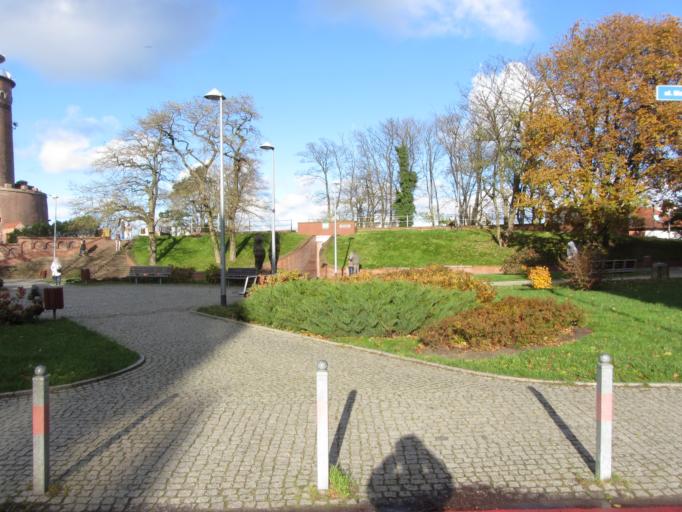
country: PL
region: West Pomeranian Voivodeship
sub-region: Powiat kolobrzeski
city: Kolobrzeg
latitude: 54.1858
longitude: 15.5551
